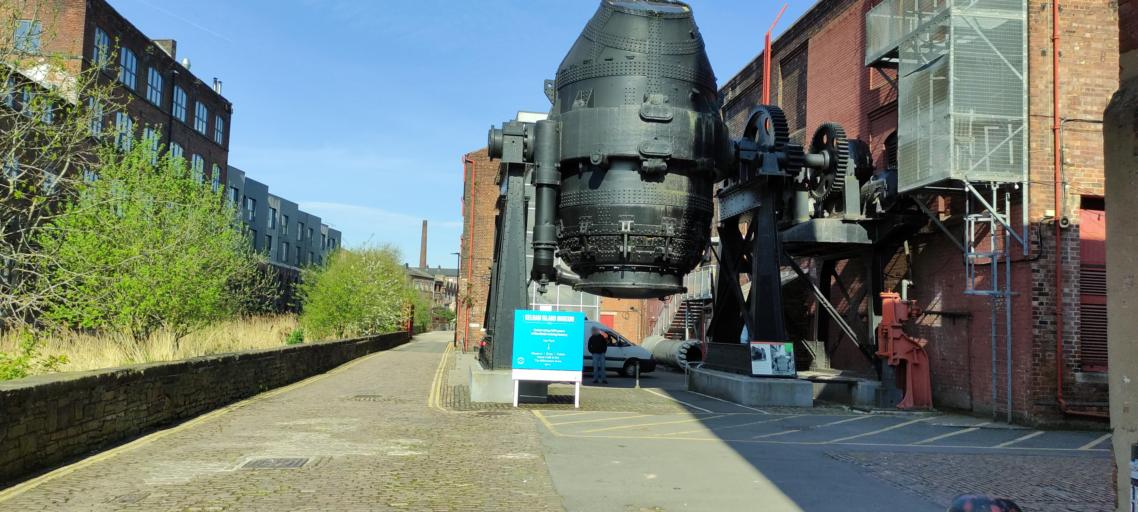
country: GB
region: England
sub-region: Sheffield
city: Sheffield
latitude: 53.3892
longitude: -1.4722
